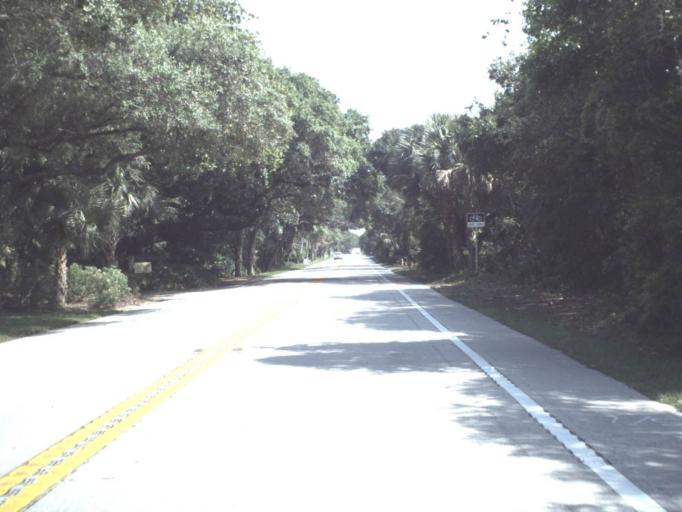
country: US
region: Florida
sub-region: Saint Johns County
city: Palm Valley
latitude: 30.1392
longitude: -81.3515
